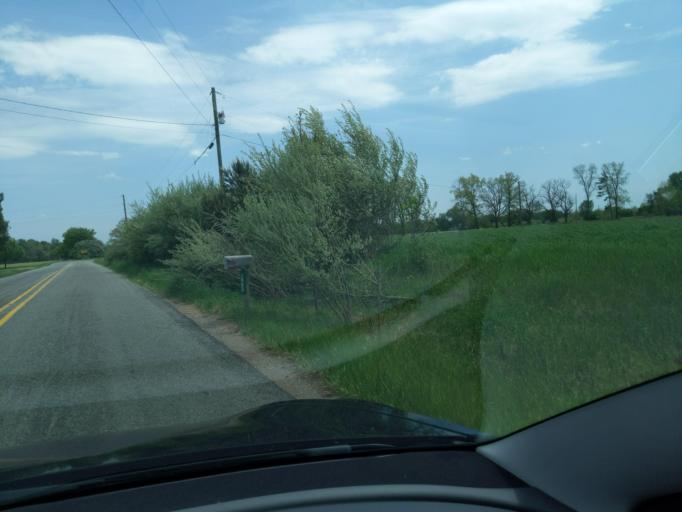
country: US
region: Michigan
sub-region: Ingham County
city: Stockbridge
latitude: 42.4685
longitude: -84.2268
